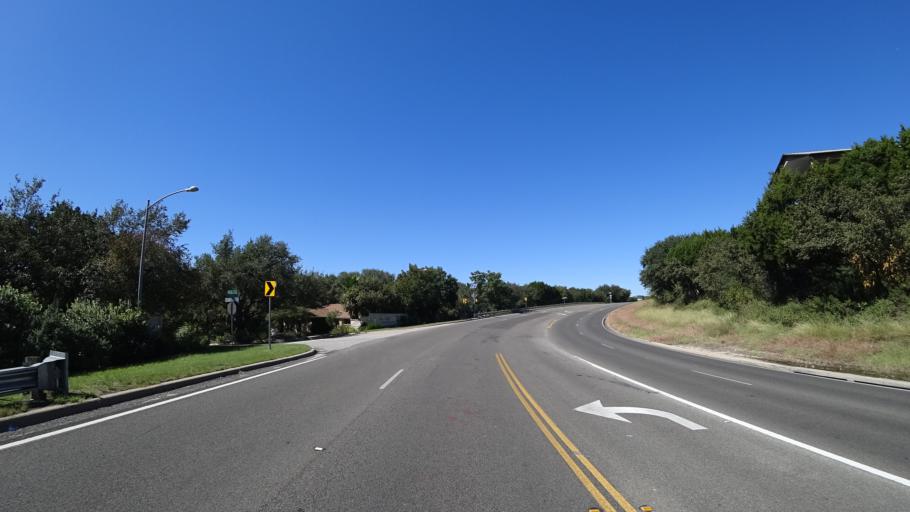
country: US
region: Texas
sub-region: Travis County
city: West Lake Hills
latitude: 30.3416
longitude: -97.7821
